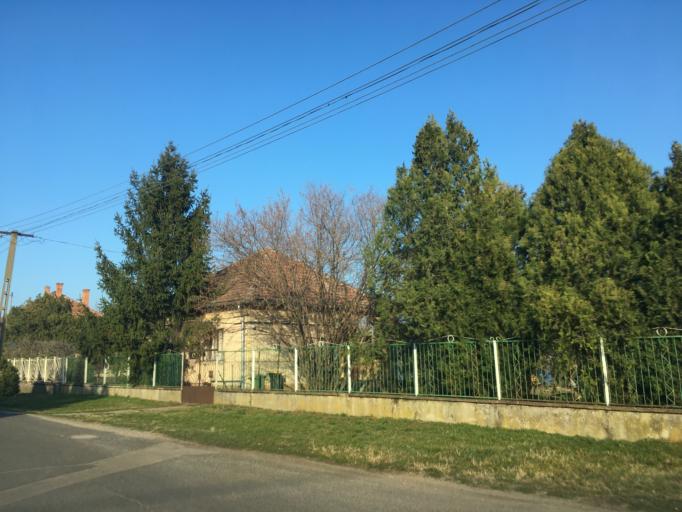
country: HU
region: Pest
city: Jaszkarajeno
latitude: 47.0166
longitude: 20.1361
